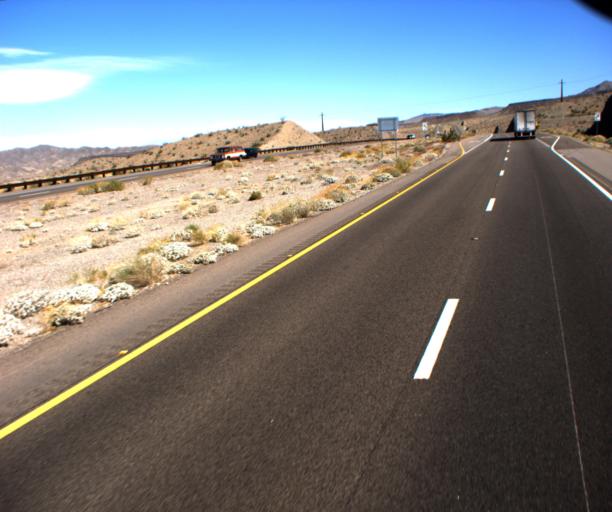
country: US
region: Nevada
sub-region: Clark County
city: Boulder City
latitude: 35.9135
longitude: -114.6289
